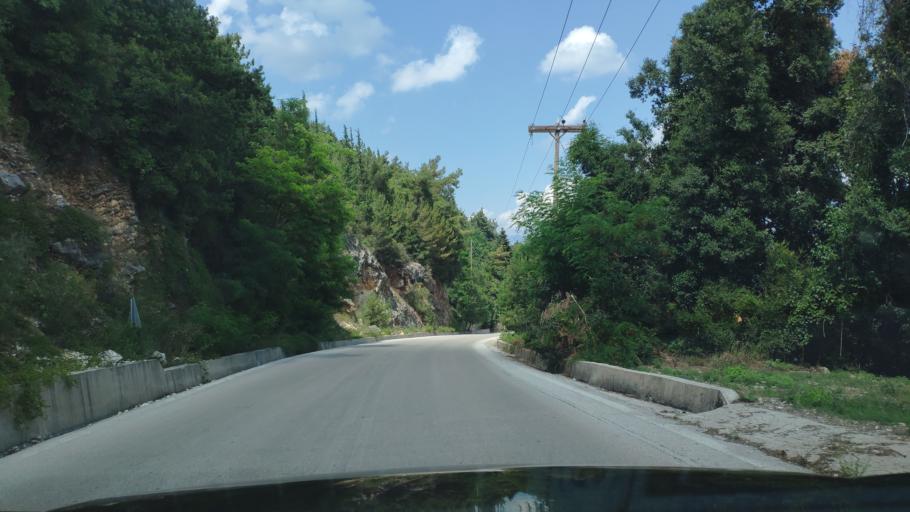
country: GR
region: Epirus
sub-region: Nomos Artas
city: Agios Dimitrios
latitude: 39.3249
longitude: 20.9953
